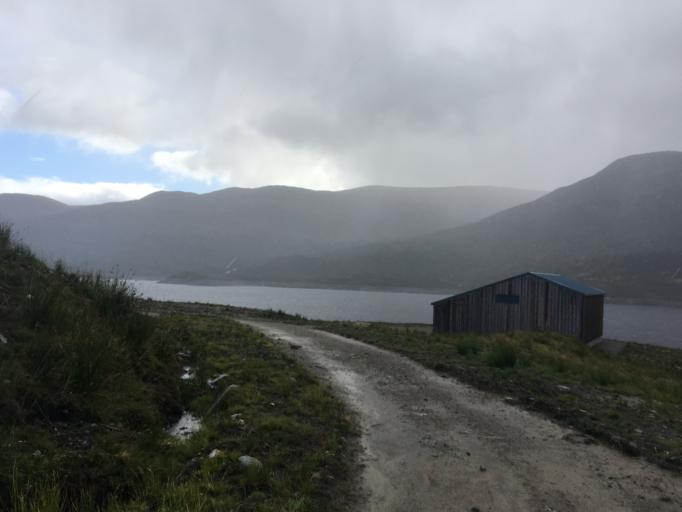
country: GB
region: Scotland
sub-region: Highland
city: Spean Bridge
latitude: 57.3420
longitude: -4.9818
